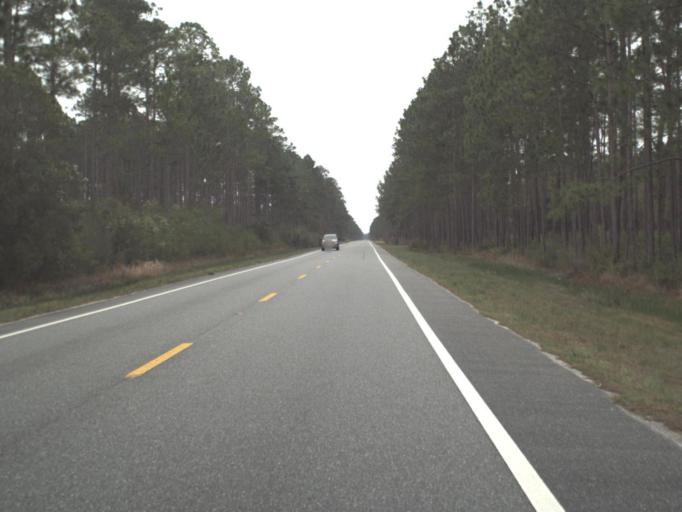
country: US
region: Florida
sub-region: Franklin County
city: Apalachicola
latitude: 29.8896
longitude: -84.9773
